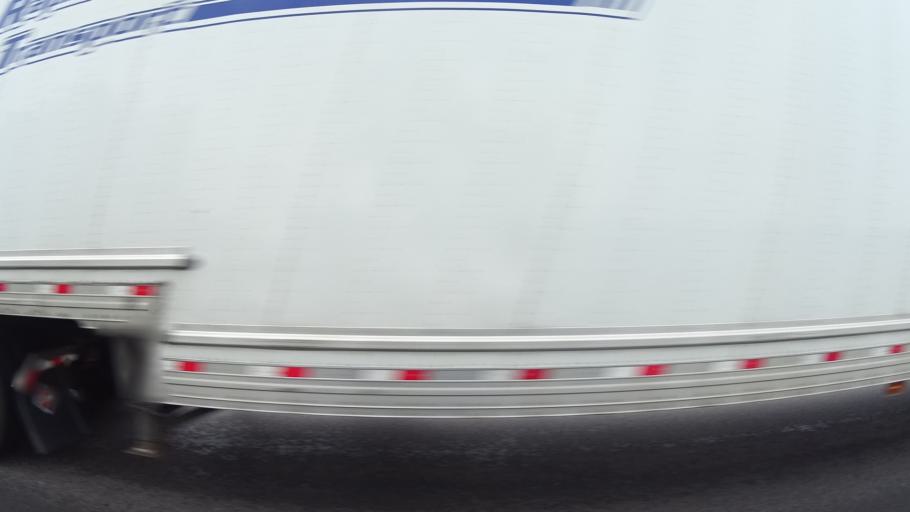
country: US
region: Ohio
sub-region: Huron County
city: Bellevue
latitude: 41.3298
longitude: -82.7644
